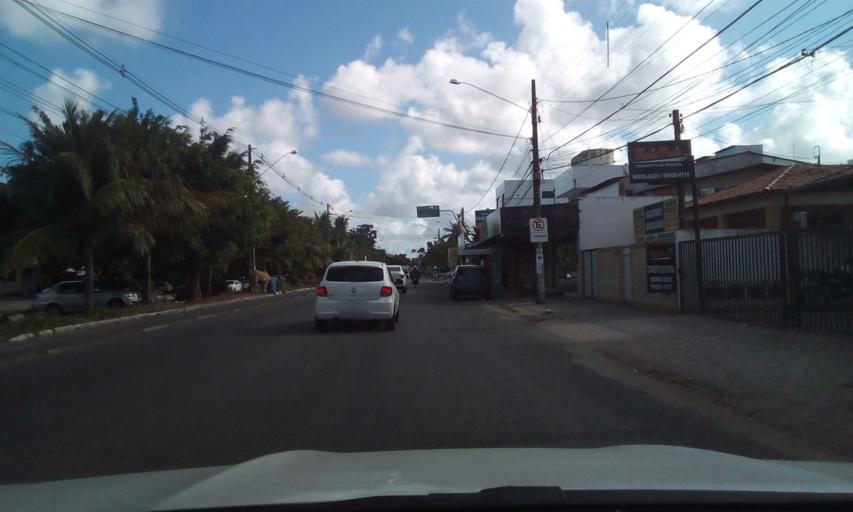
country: BR
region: Paraiba
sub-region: Joao Pessoa
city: Joao Pessoa
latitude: -7.1741
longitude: -34.8368
